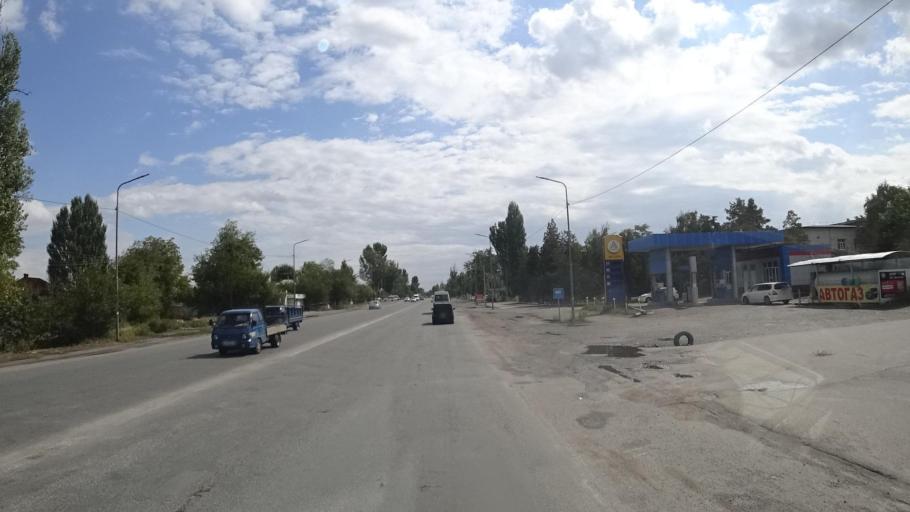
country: KG
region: Chuy
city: Lebedinovka
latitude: 42.8847
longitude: 74.6838
